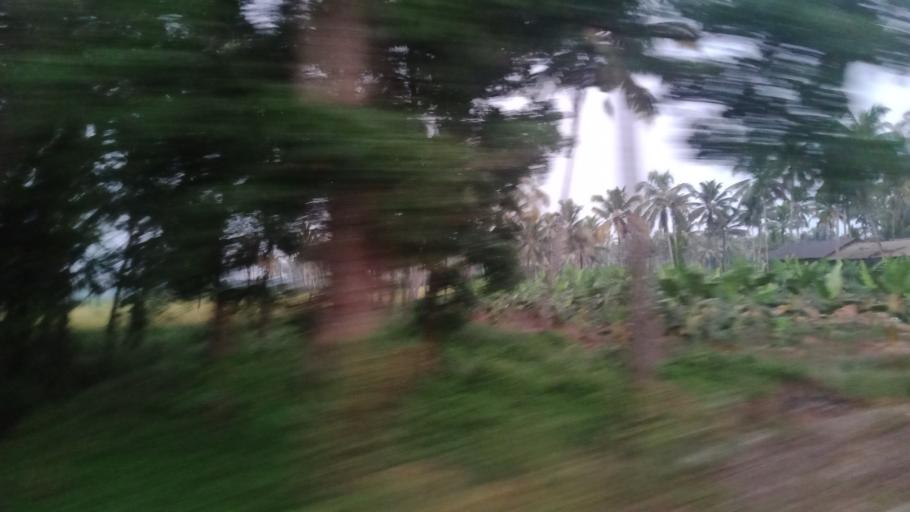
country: IN
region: Kerala
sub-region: Ernakulam
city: Angamali
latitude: 10.1962
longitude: 76.3084
